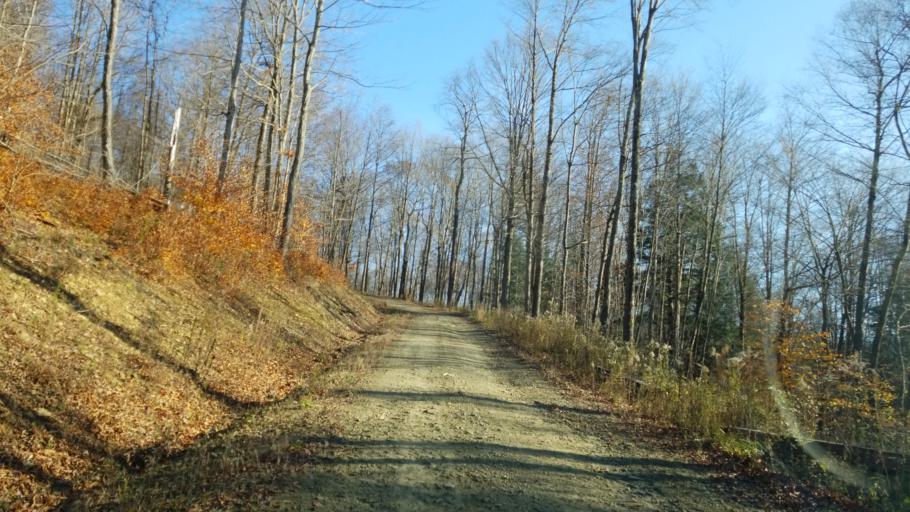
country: US
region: Pennsylvania
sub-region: Clearfield County
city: Treasure Lake
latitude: 41.1570
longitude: -78.6570
